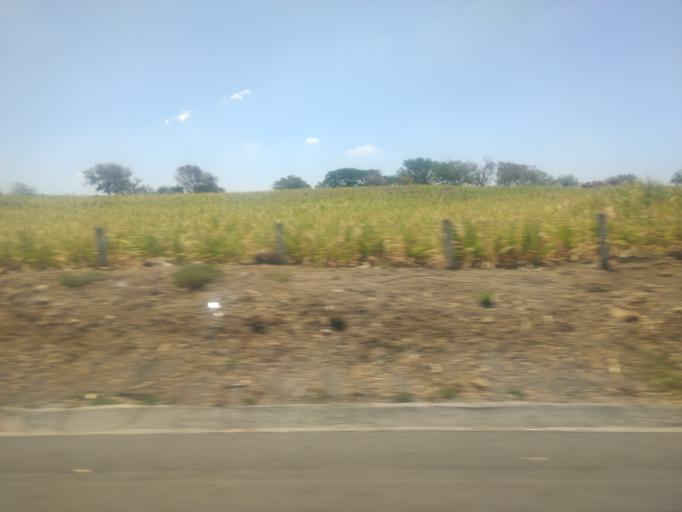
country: MX
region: Colima
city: Cuauhtemoc
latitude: 19.3227
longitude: -103.5905
